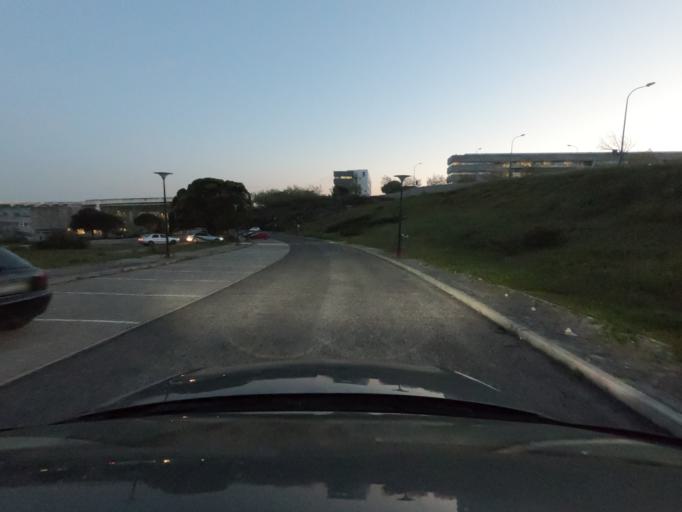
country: PT
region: Lisbon
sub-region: Oeiras
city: Porto Salvo
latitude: 38.7391
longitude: -9.3031
